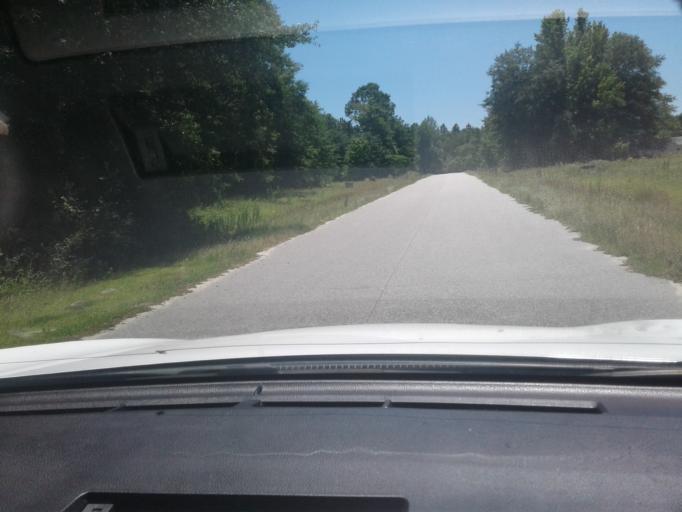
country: US
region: North Carolina
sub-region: Harnett County
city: Walkertown
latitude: 35.3366
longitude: -78.9165
